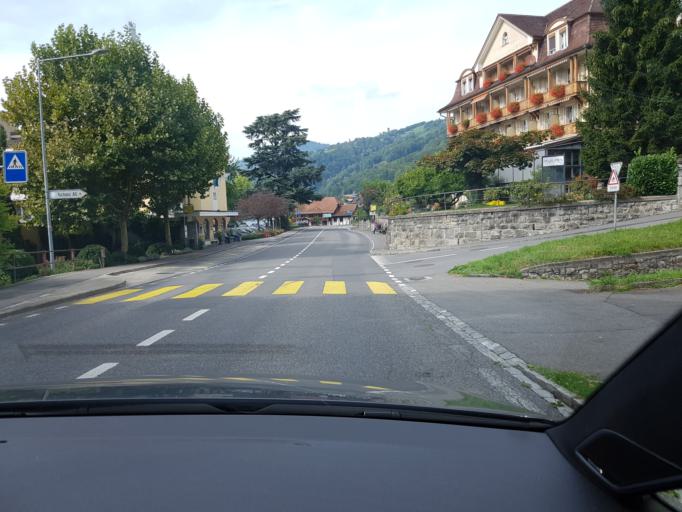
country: CH
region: Bern
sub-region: Thun District
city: Sigriswil
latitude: 46.6958
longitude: 7.7384
